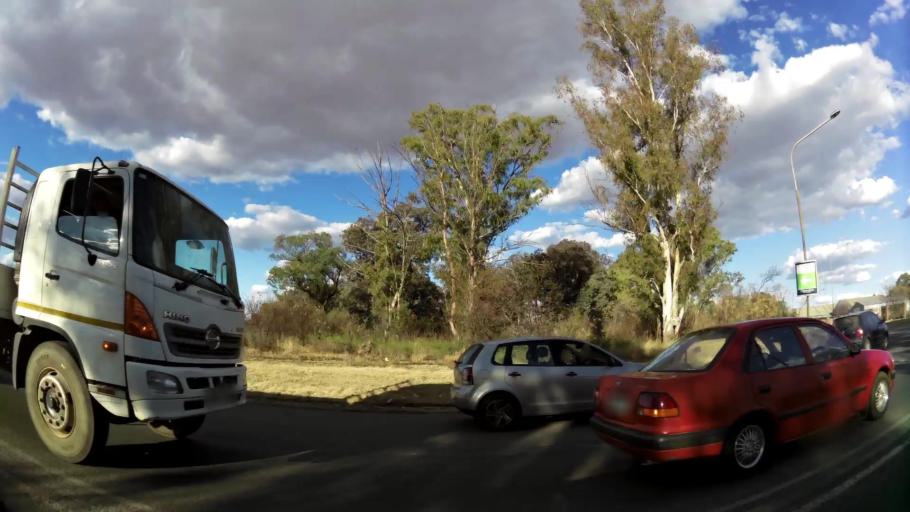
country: ZA
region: North-West
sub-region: Dr Kenneth Kaunda District Municipality
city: Potchefstroom
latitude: -26.7084
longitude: 27.0776
